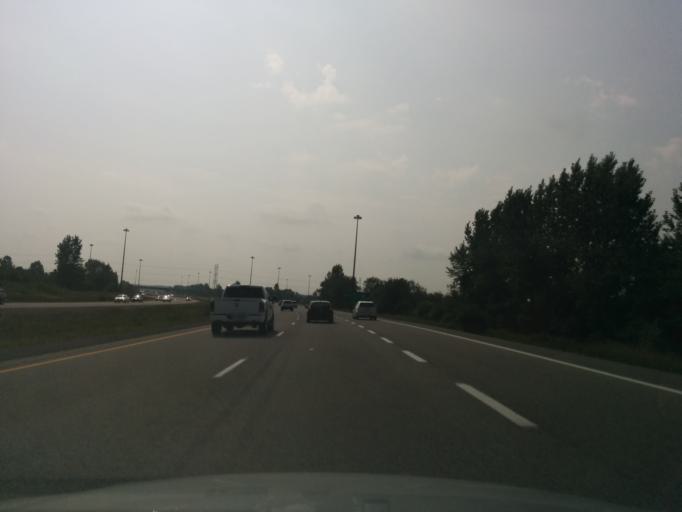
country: CA
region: Ontario
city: Bells Corners
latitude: 45.3188
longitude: -75.8056
